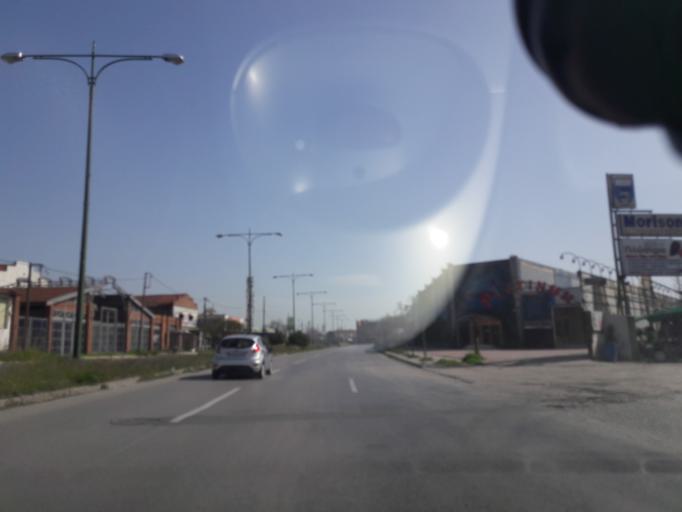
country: GR
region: Central Macedonia
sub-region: Nomos Thessalonikis
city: Menemeni
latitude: 40.6460
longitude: 22.9085
